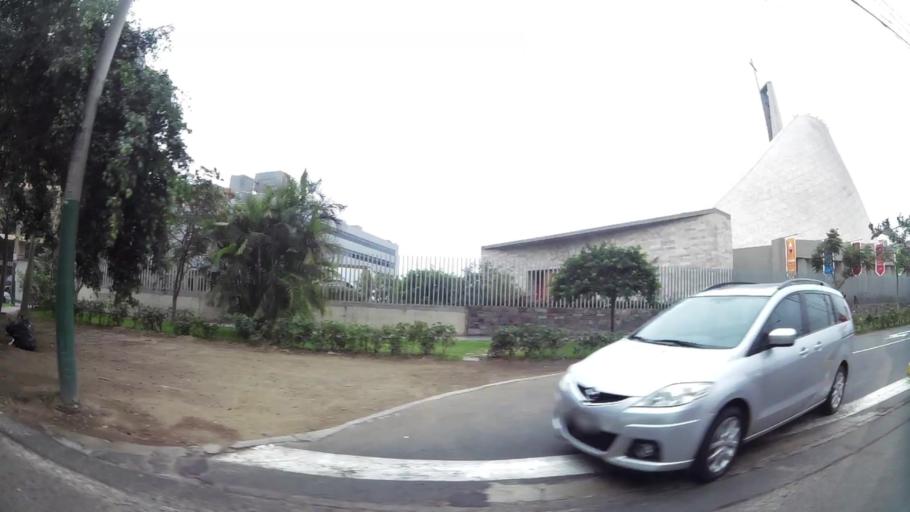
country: PE
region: Lima
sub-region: Lima
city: San Luis
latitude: -12.1010
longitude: -76.9769
